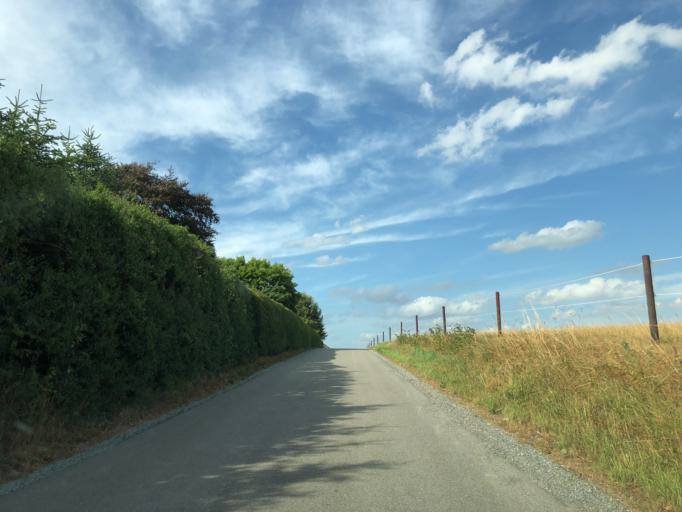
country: DK
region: South Denmark
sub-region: Vejle Kommune
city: Egtved
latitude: 55.6732
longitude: 9.3032
